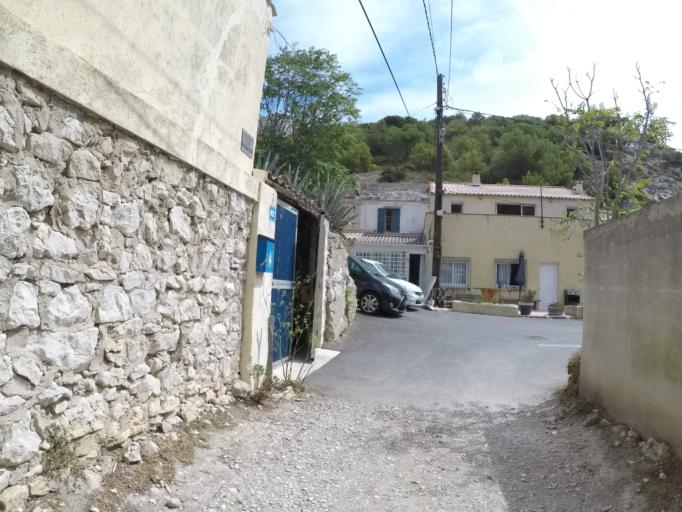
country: FR
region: Provence-Alpes-Cote d'Azur
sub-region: Departement des Bouches-du-Rhone
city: Marseille 08
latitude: 43.2139
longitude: 5.3554
